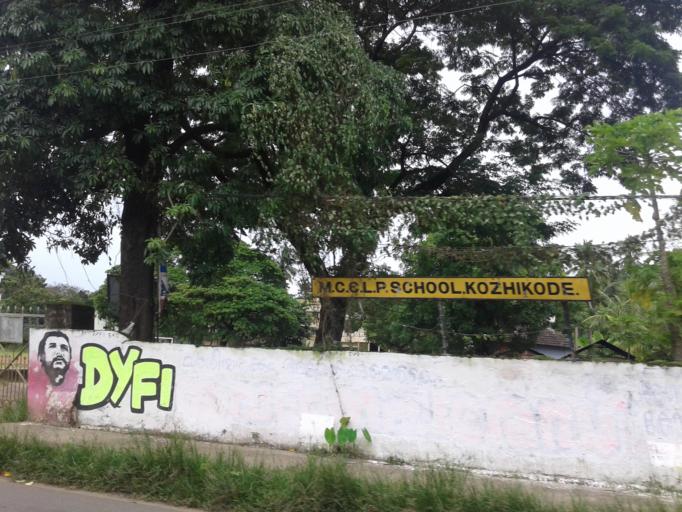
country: IN
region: Kerala
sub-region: Kozhikode
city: Kozhikode
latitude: 11.2631
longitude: 75.7774
